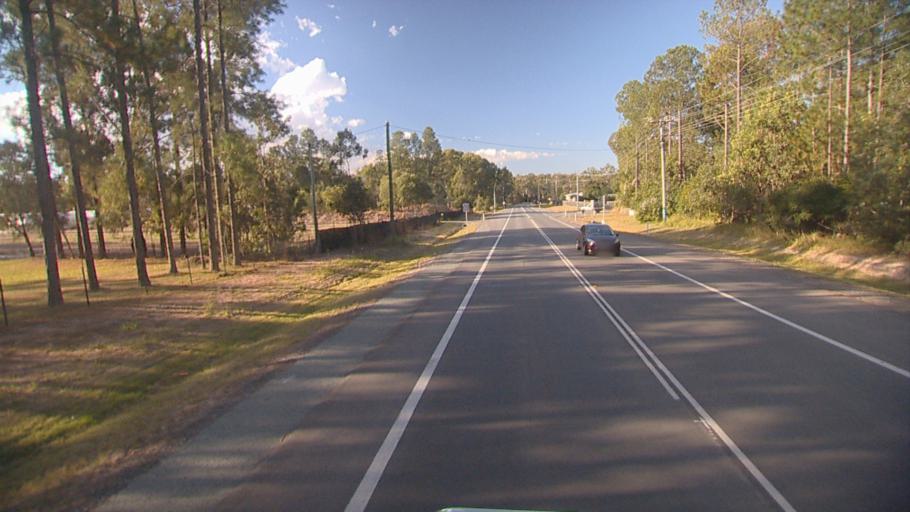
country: AU
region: Queensland
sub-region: Logan
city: Park Ridge South
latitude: -27.7187
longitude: 152.9694
